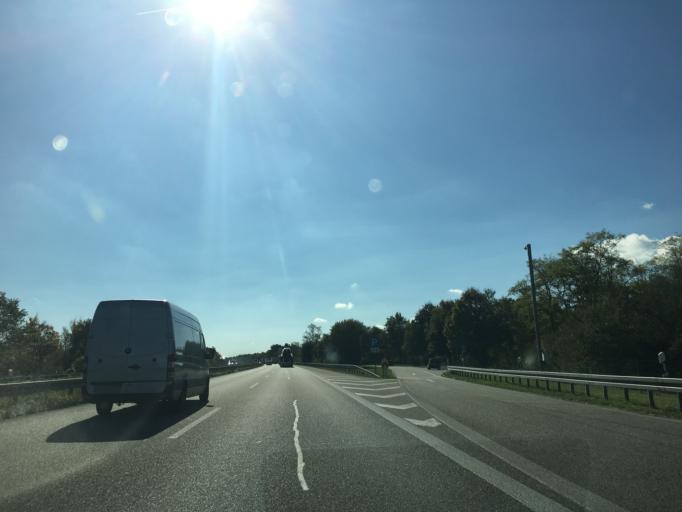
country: FR
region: Alsace
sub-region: Departement du Haut-Rhin
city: Blodelsheim
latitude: 47.8746
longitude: 7.5697
